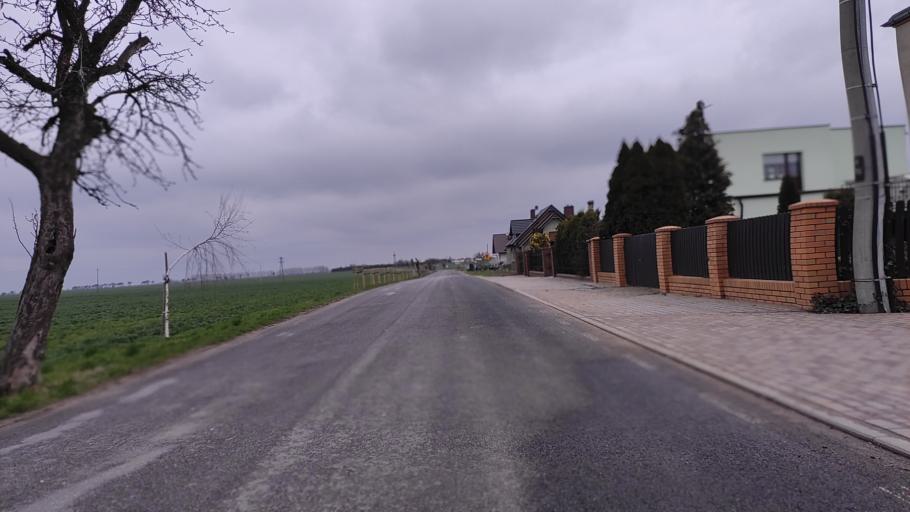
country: PL
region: Greater Poland Voivodeship
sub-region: Powiat poznanski
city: Kostrzyn
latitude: 52.4042
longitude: 17.1645
